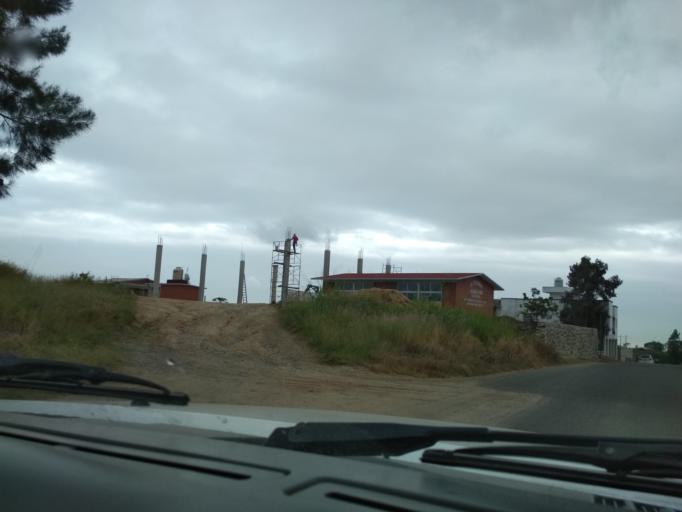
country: MX
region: Veracruz
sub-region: Emiliano Zapata
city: Dos Rios
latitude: 19.5205
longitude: -96.7951
